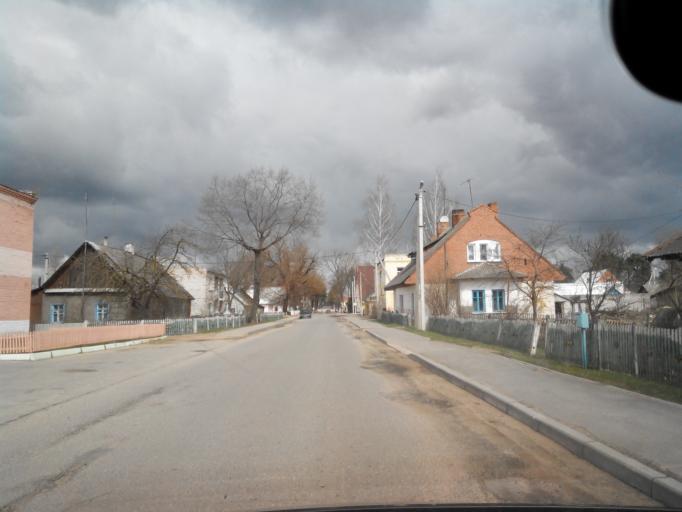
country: BY
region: Vitebsk
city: Mosar
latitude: 55.1427
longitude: 27.2074
